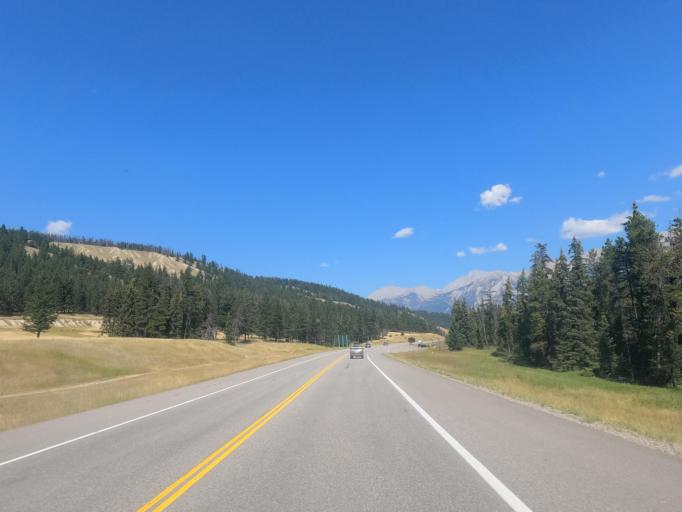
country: CA
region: Alberta
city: Jasper Park Lodge
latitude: 52.9029
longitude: -118.0654
